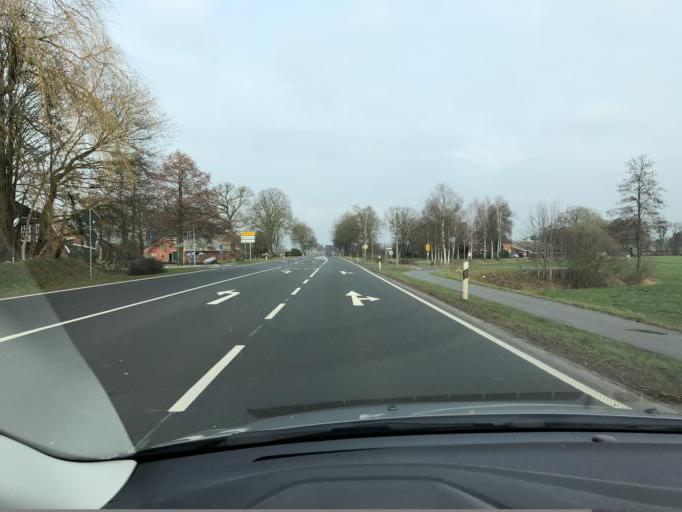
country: DE
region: Lower Saxony
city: Mittegrossefehn
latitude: 53.3737
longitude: 7.5849
